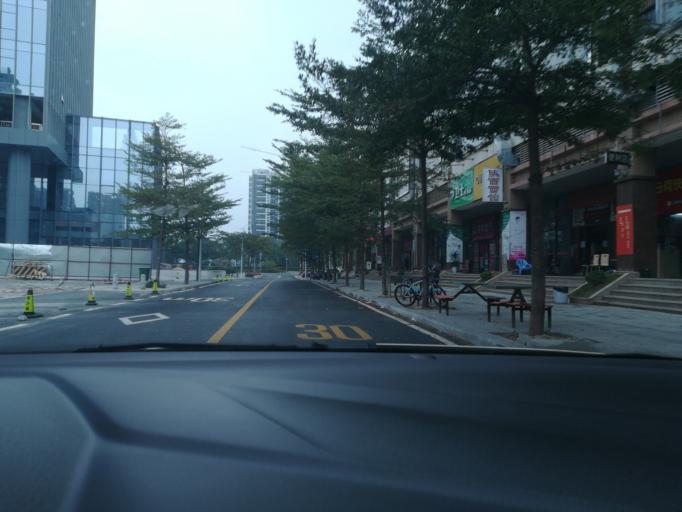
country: CN
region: Guangdong
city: Nansha
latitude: 22.8017
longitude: 113.5339
